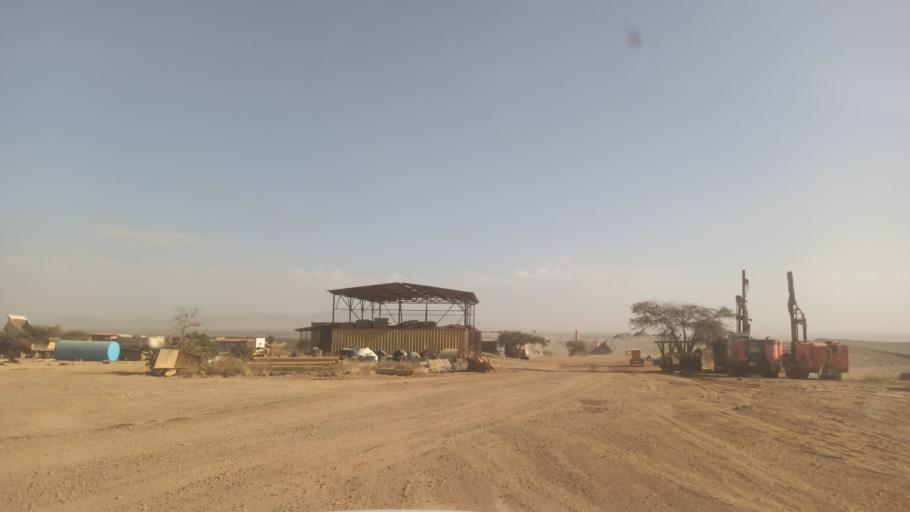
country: ET
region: Oromiya
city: Ziway
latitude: 7.9357
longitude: 38.6143
